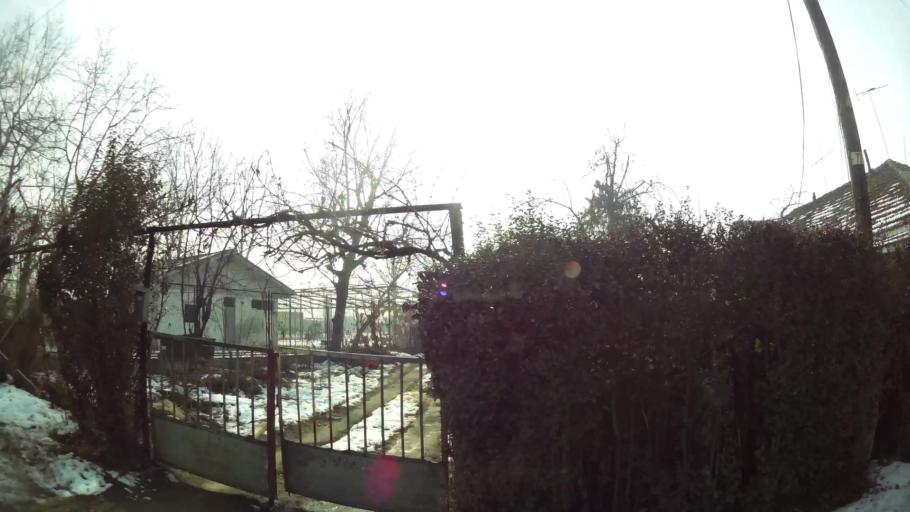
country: MK
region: Kisela Voda
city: Kisela Voda
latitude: 41.9915
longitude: 21.5020
